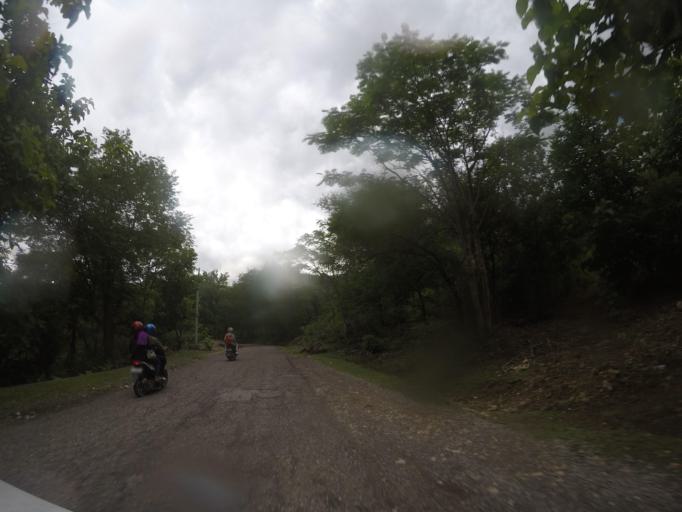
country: ID
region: East Nusa Tenggara
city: Atambua
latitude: -8.9670
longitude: 125.0133
